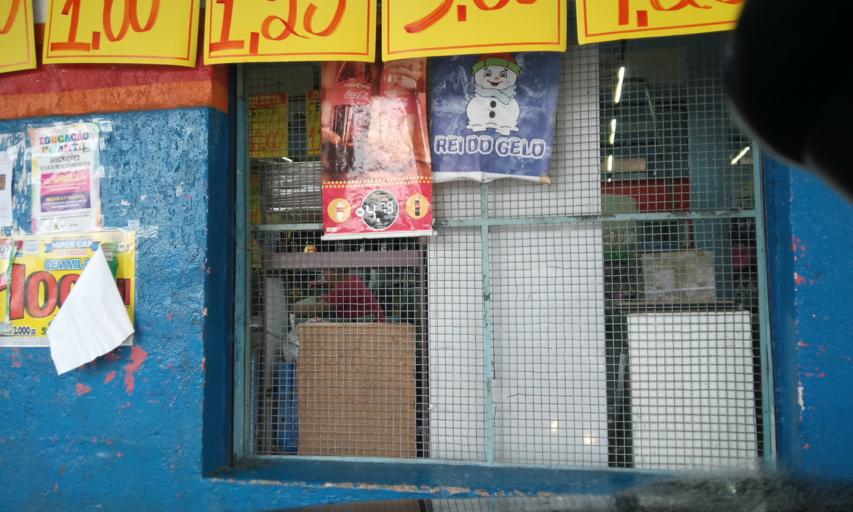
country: BR
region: Sao Paulo
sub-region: Maua
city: Maua
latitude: -23.7404
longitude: -46.4959
